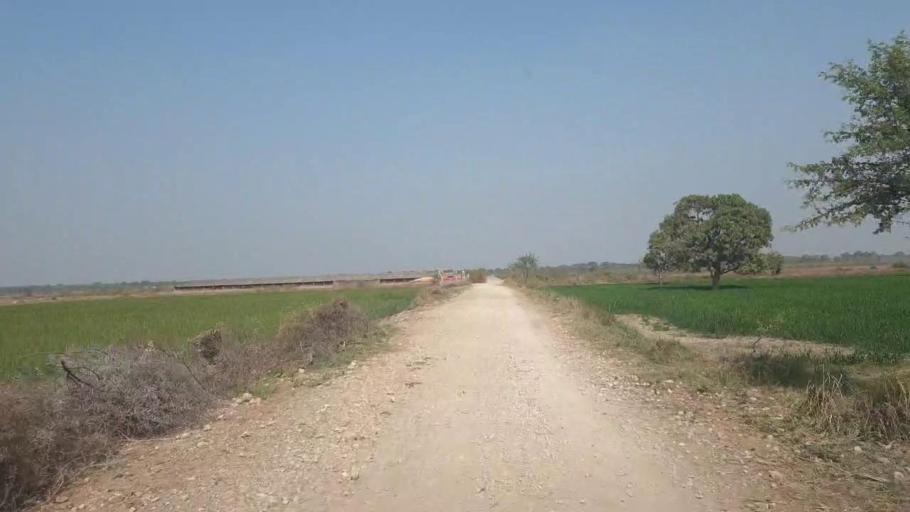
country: PK
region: Sindh
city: Tando Allahyar
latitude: 25.4385
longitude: 68.8360
